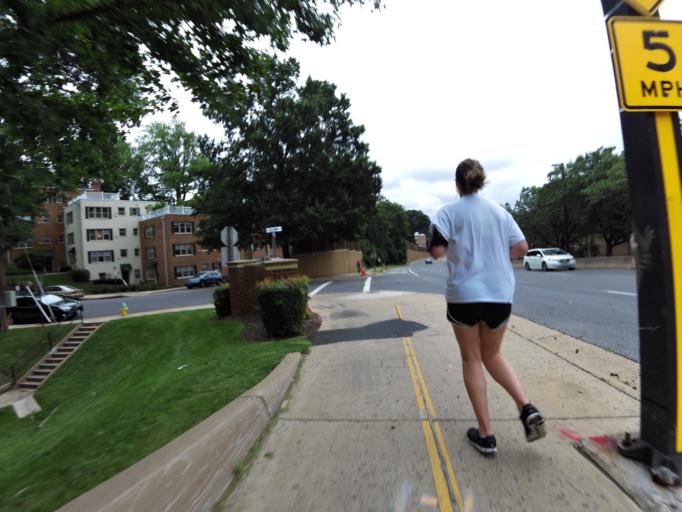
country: US
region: Virginia
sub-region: Arlington County
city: Arlington
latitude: 38.8979
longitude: -77.0795
